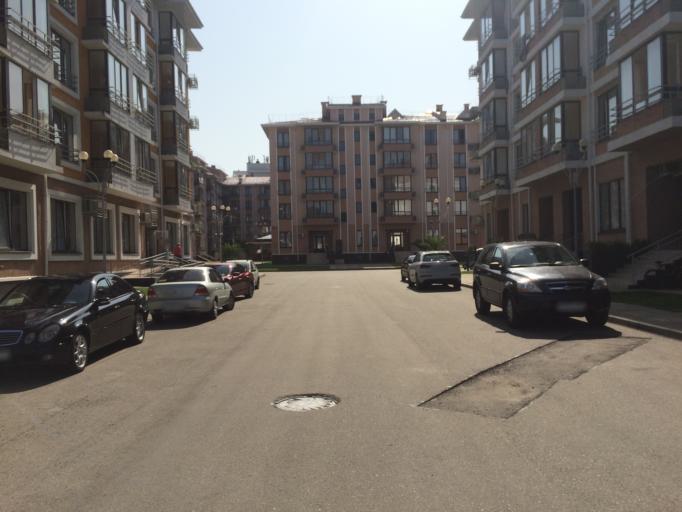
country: RU
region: Krasnodarskiy
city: Adler
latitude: 43.3968
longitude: 39.9782
